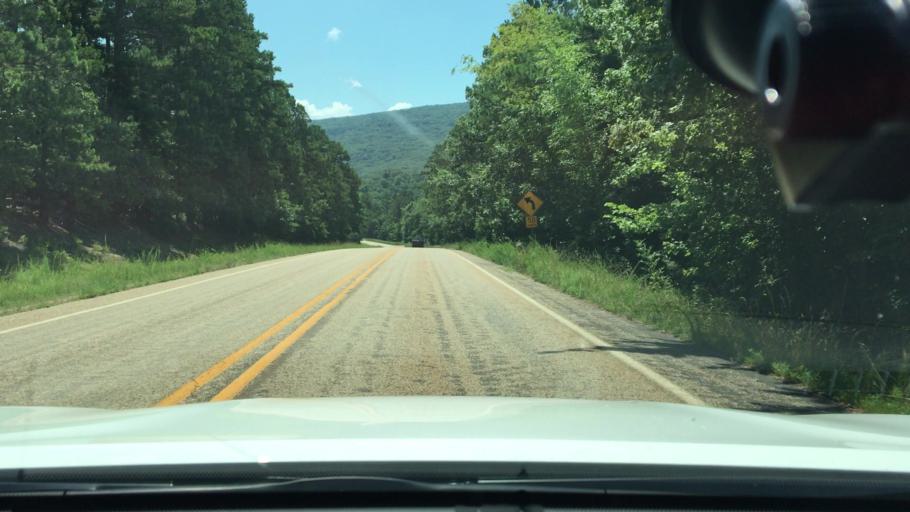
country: US
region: Arkansas
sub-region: Logan County
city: Paris
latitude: 35.1954
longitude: -93.6327
